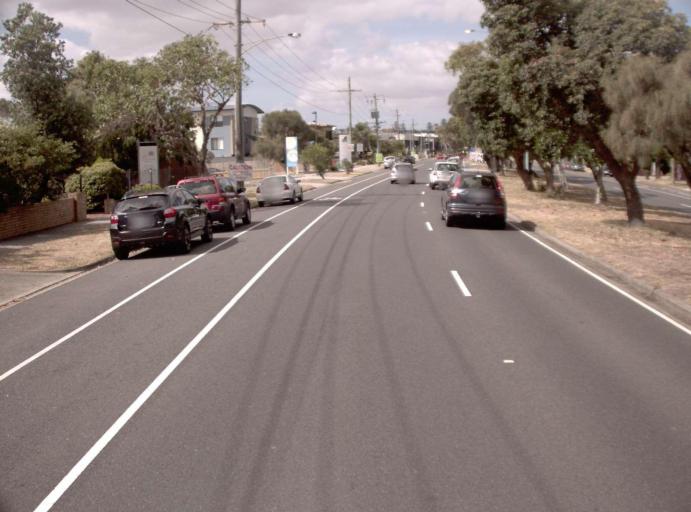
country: AU
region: Victoria
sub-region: Frankston
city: Frankston
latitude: -38.1361
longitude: 145.1242
